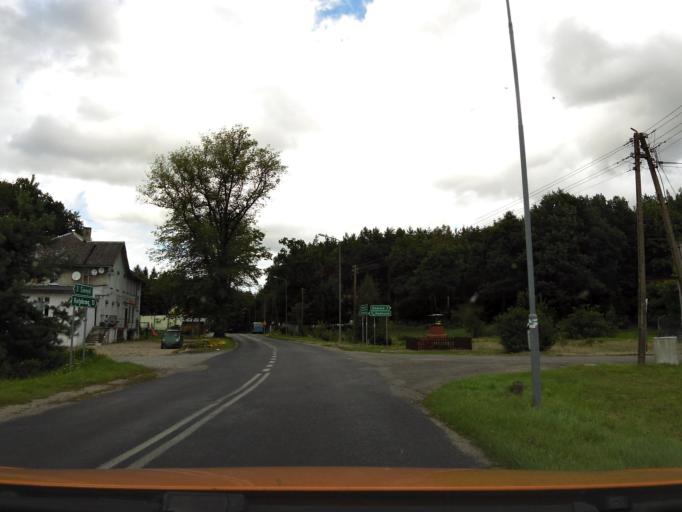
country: PL
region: West Pomeranian Voivodeship
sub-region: Powiat kolobrzeski
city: Goscino
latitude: 54.0555
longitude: 15.5503
